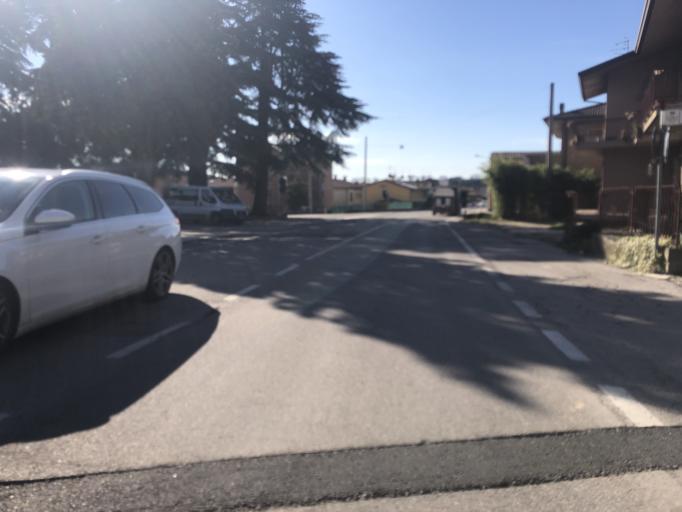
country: IT
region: Veneto
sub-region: Provincia di Verona
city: Sant'Ambrogio di Valpollicella
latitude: 45.5247
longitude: 10.8385
